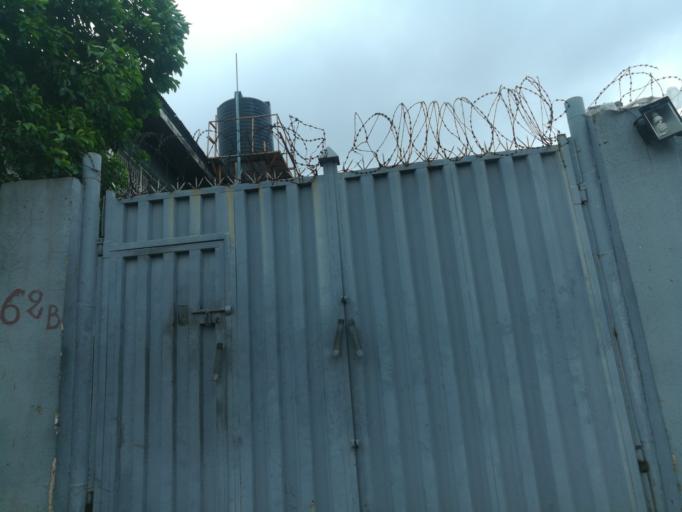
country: NG
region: Lagos
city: Somolu
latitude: 6.5551
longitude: 3.3625
